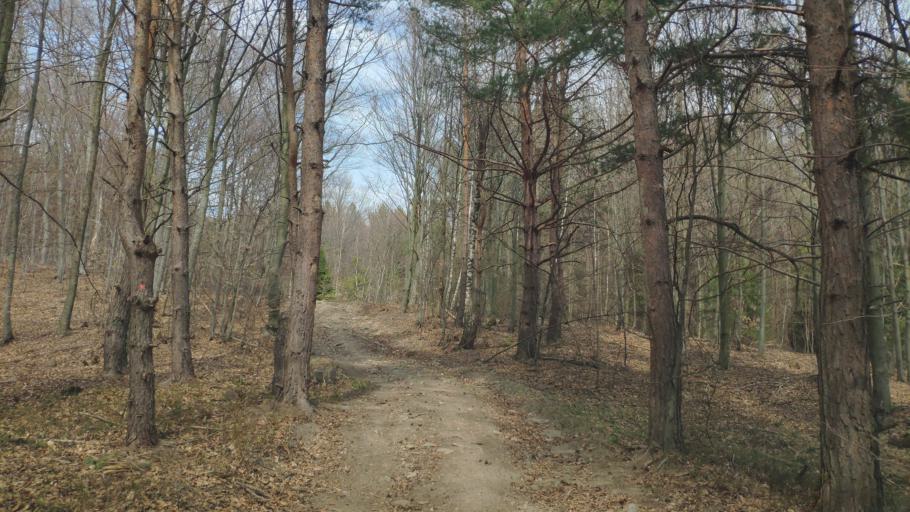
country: SK
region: Kosicky
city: Gelnica
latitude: 48.7529
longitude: 21.0207
